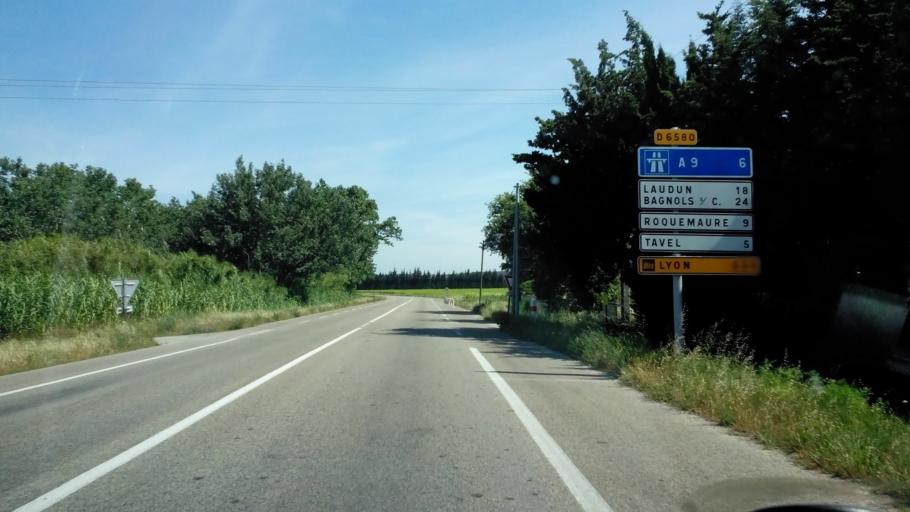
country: FR
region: Languedoc-Roussillon
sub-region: Departement du Gard
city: Les Angles
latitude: 43.9792
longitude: 4.7485
